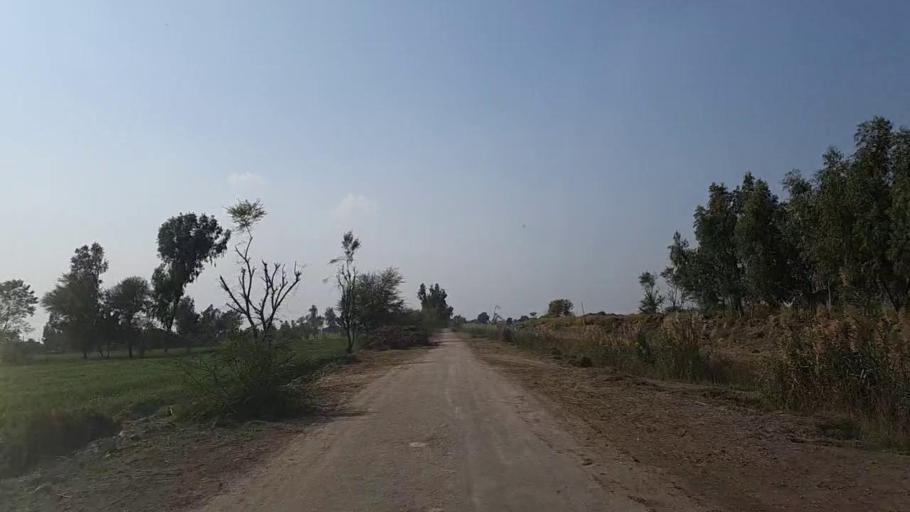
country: PK
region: Sindh
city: Jam Sahib
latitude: 26.2884
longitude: 68.5717
